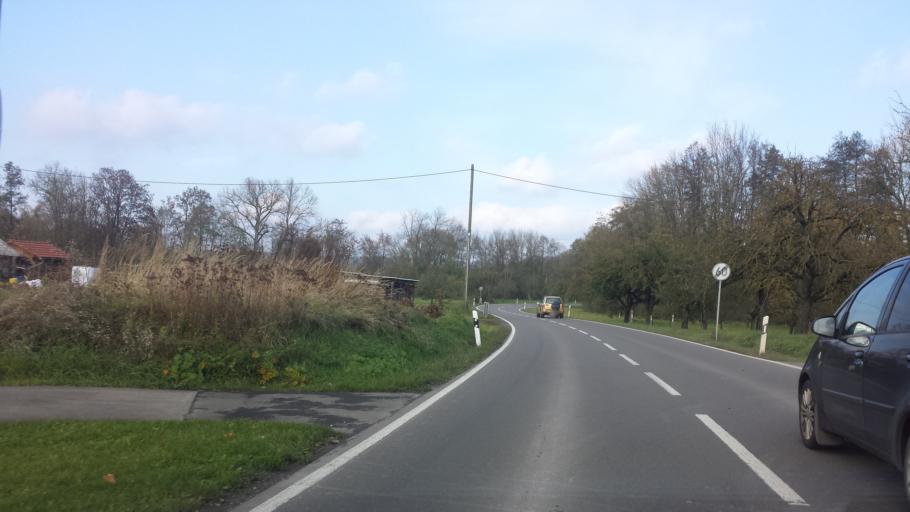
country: DE
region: Baden-Wuerttemberg
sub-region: Karlsruhe Region
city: Zaisenhausen
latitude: 49.1096
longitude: 8.7453
